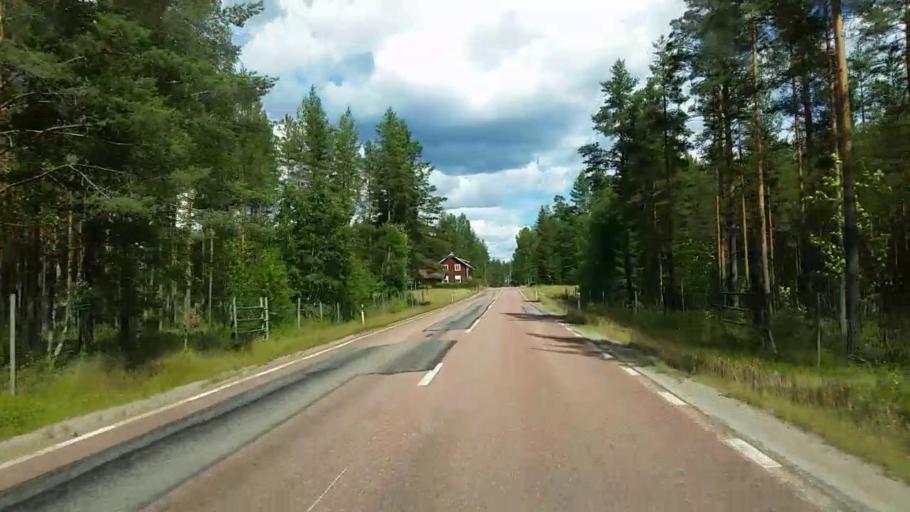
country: SE
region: Gaevleborg
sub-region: Ovanakers Kommun
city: Edsbyn
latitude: 61.3559
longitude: 15.6935
